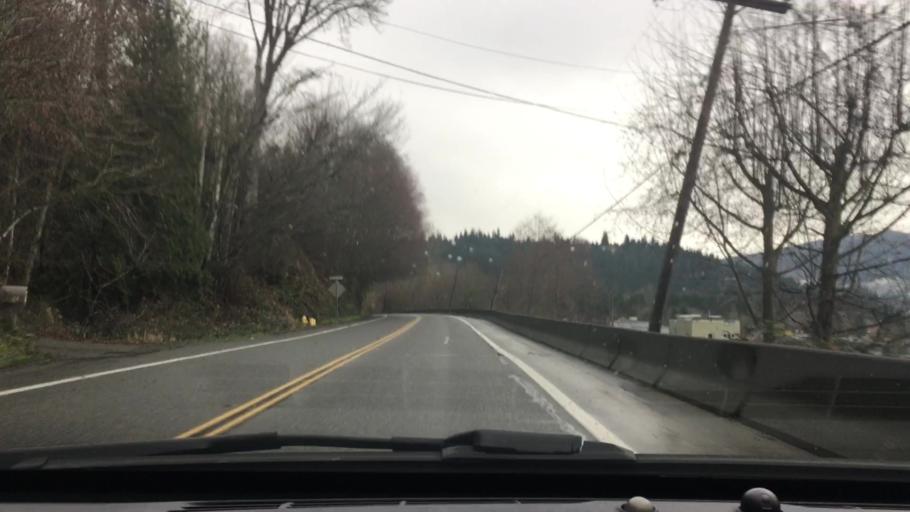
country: US
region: Washington
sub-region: King County
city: West Lake Sammamish
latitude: 47.5695
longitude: -122.0626
